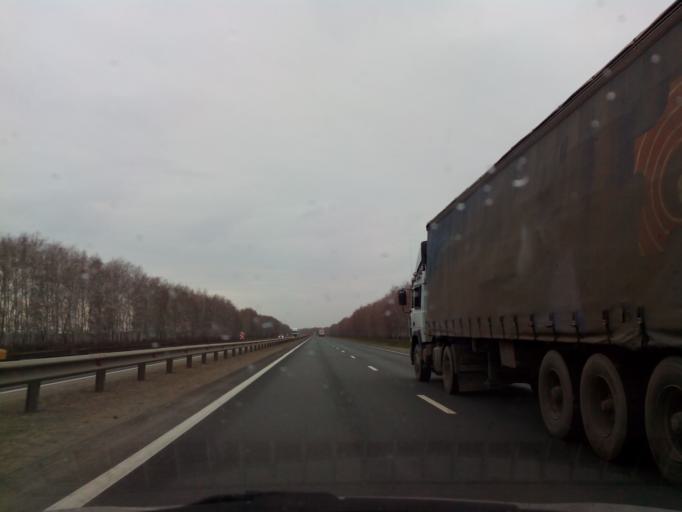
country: RU
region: Tambov
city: Selezni
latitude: 52.7625
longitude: 41.1221
